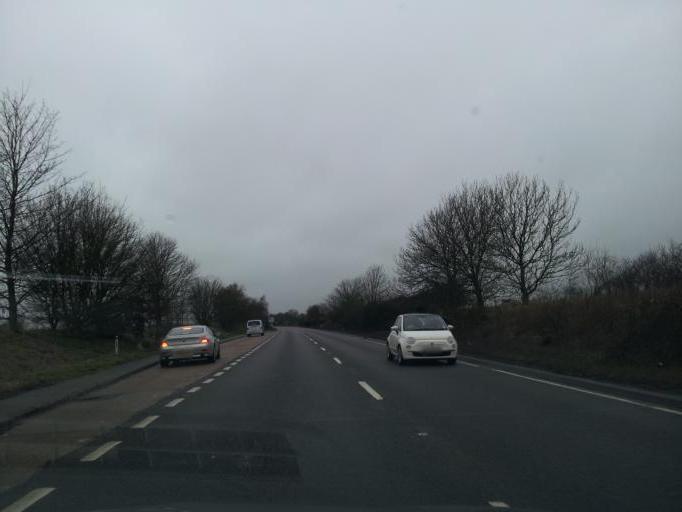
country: GB
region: England
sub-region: Essex
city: Mistley
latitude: 51.9075
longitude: 1.1083
